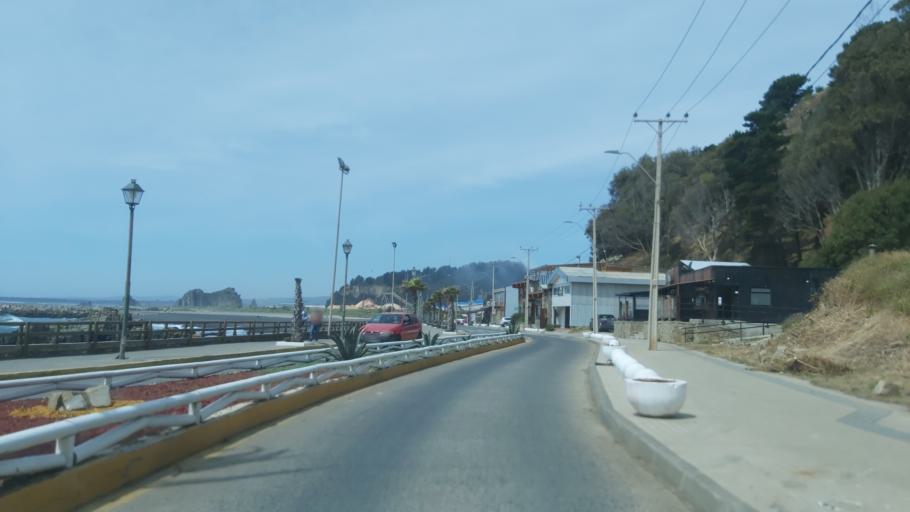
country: CL
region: Maule
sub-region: Provincia de Talca
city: Constitucion
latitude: -35.3265
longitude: -72.4285
